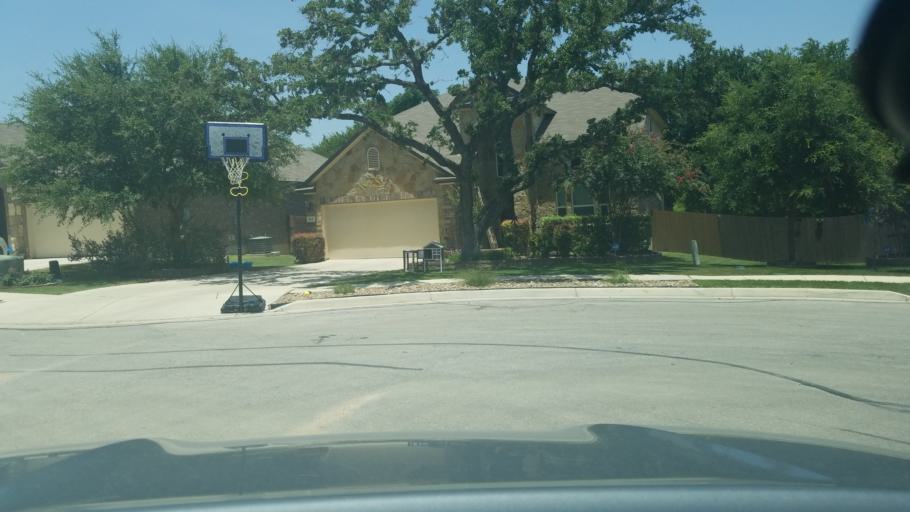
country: US
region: Texas
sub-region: Guadalupe County
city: Cibolo
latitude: 29.5815
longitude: -98.2273
